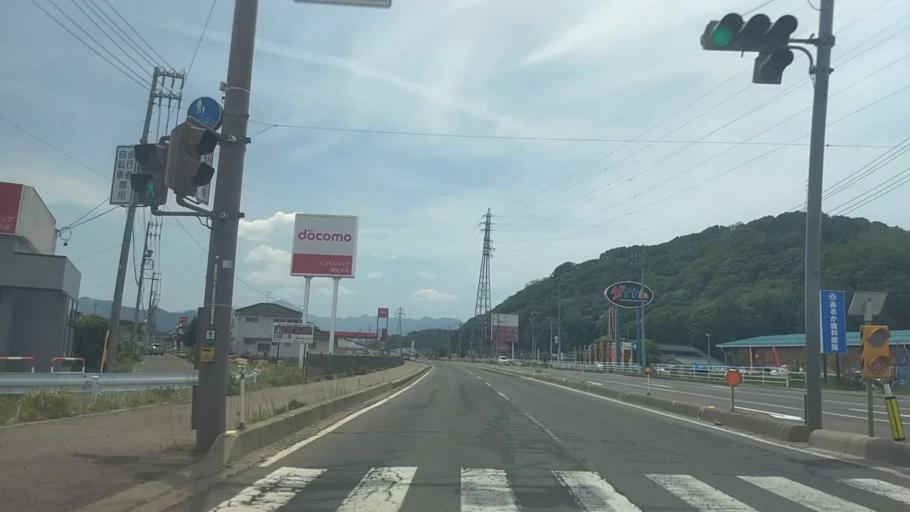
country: JP
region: Nagano
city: Saku
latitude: 36.2042
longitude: 138.4681
